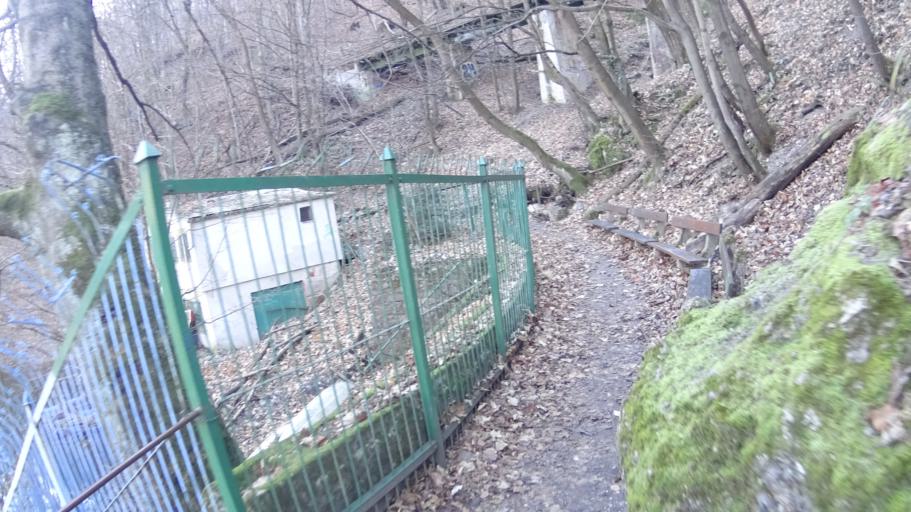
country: HU
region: Borsod-Abauj-Zemplen
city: Sajobabony
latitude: 48.1060
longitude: 20.6180
